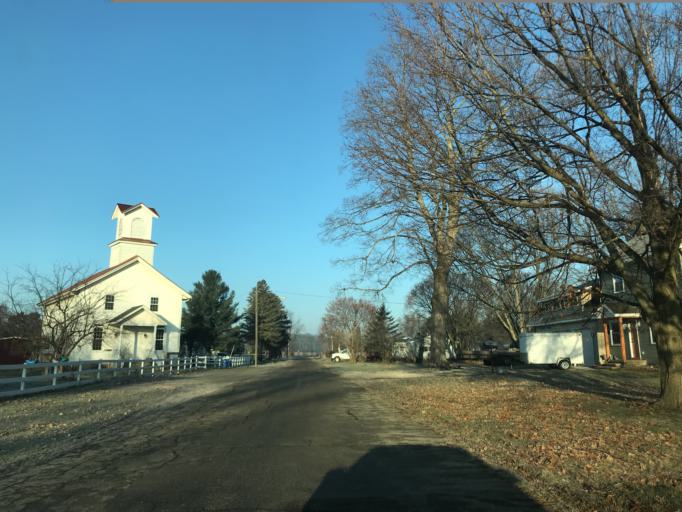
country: US
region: Michigan
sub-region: Eaton County
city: Eaton Rapids
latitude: 42.4447
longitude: -84.5644
